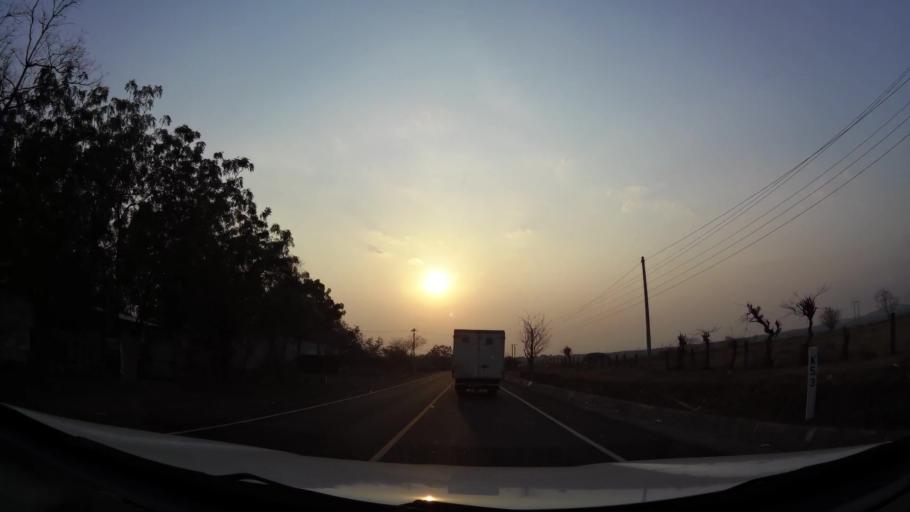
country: NI
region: Leon
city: La Paz Centro
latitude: 12.3304
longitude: -86.6436
